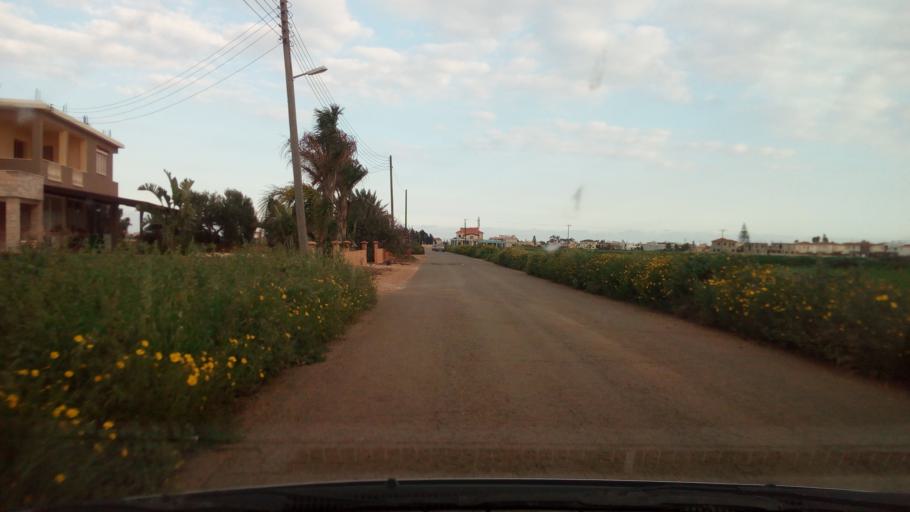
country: CY
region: Ammochostos
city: Avgorou
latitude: 34.9819
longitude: 33.8402
